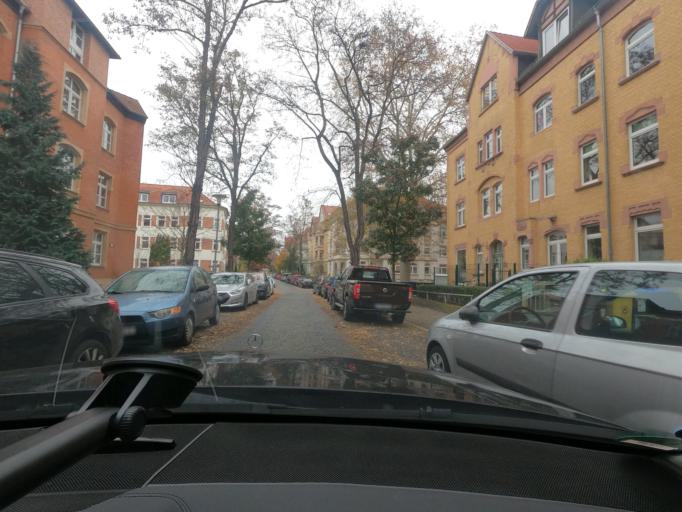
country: DE
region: Thuringia
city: Erfurt
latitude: 50.9661
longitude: 11.0369
